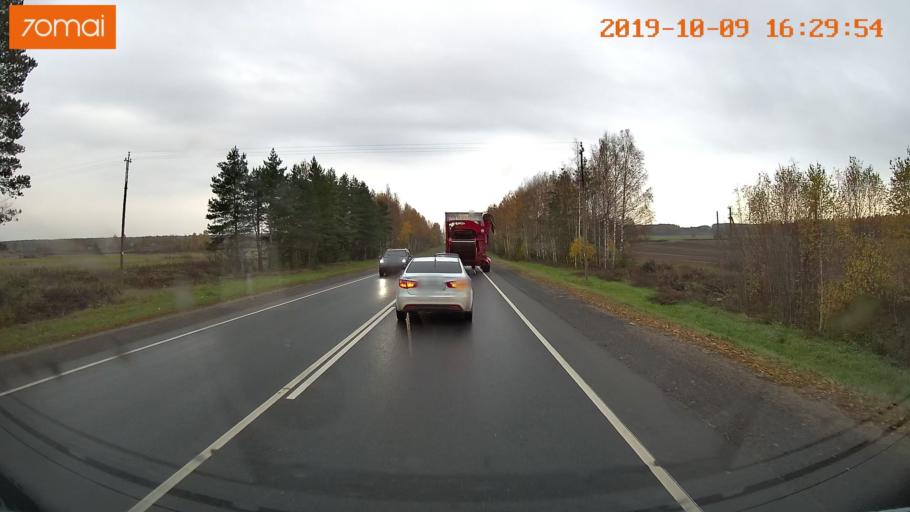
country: RU
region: Kostroma
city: Oktyabr'skiy
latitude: 57.6221
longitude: 40.9377
